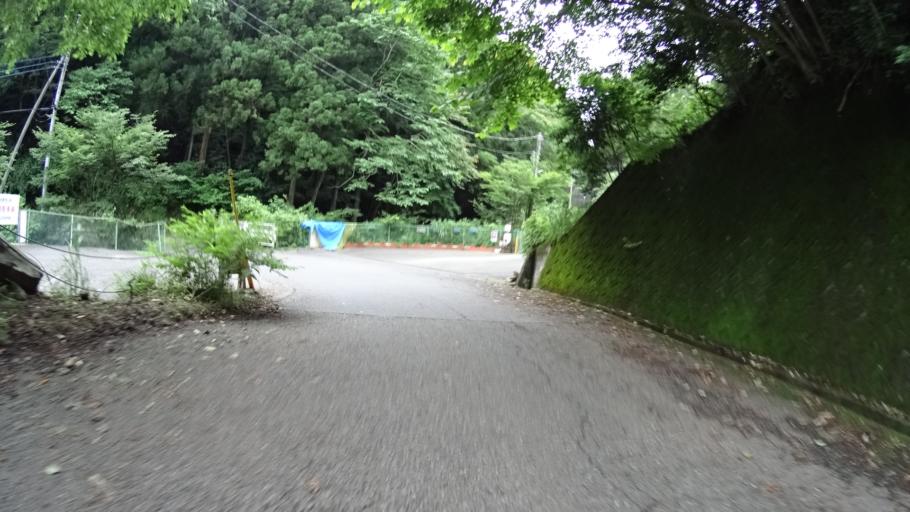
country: JP
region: Kanagawa
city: Atsugi
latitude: 35.5012
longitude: 139.2643
